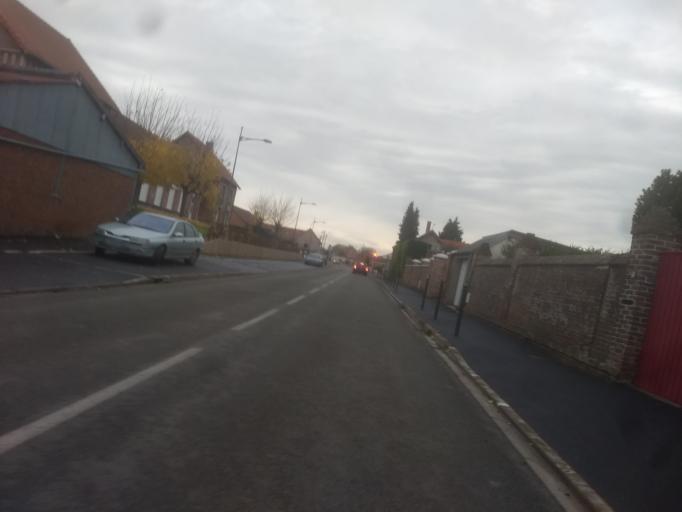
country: FR
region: Nord-Pas-de-Calais
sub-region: Departement du Pas-de-Calais
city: Dainville
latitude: 50.2463
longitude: 2.7244
